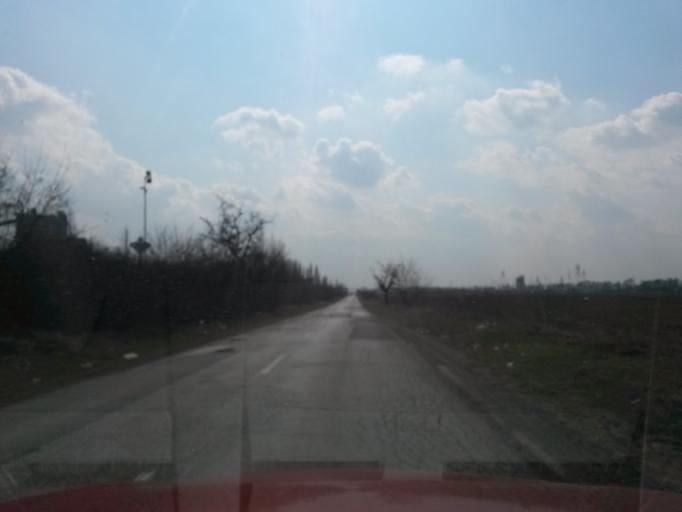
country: SK
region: Kosicky
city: Kosice
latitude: 48.6147
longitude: 21.1783
